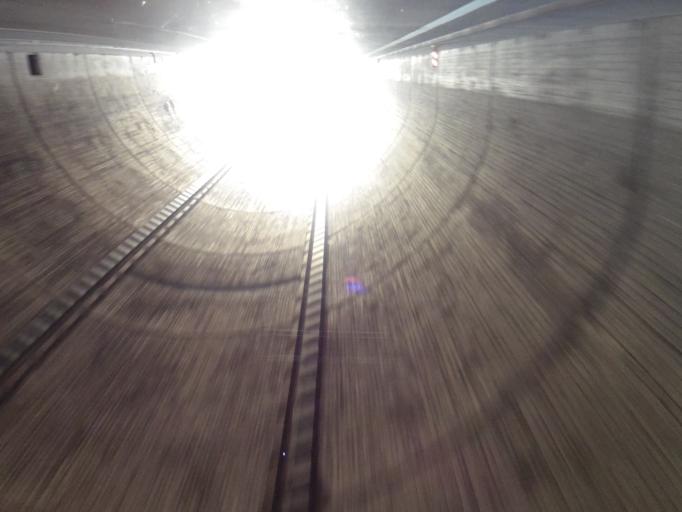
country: DE
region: Baden-Wuerttemberg
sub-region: Regierungsbezirk Stuttgart
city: Aichelberg
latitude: 48.6283
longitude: 9.5749
